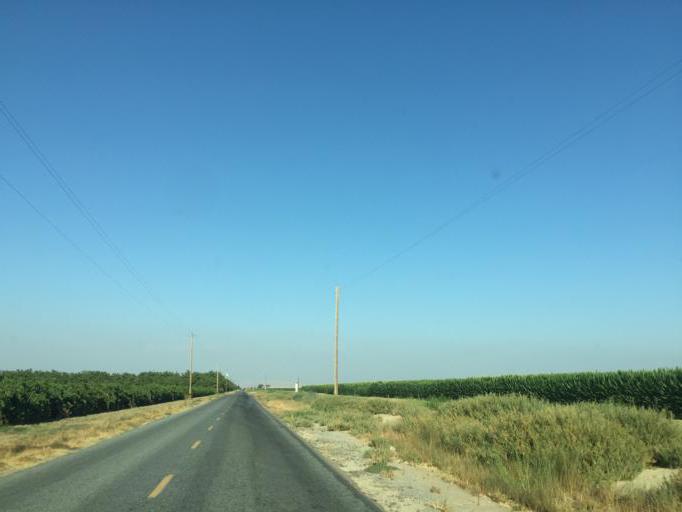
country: US
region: California
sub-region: Tulare County
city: London
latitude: 36.4582
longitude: -119.4201
